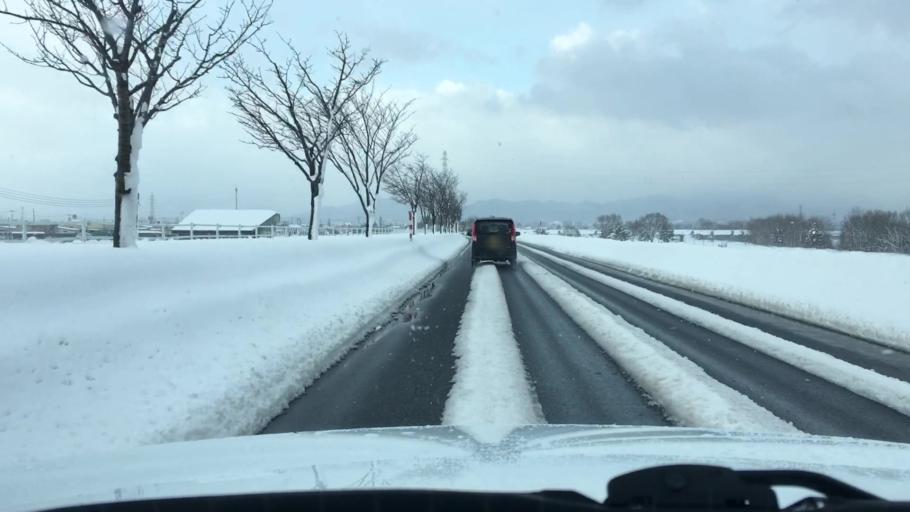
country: JP
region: Aomori
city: Hirosaki
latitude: 40.6330
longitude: 140.4726
